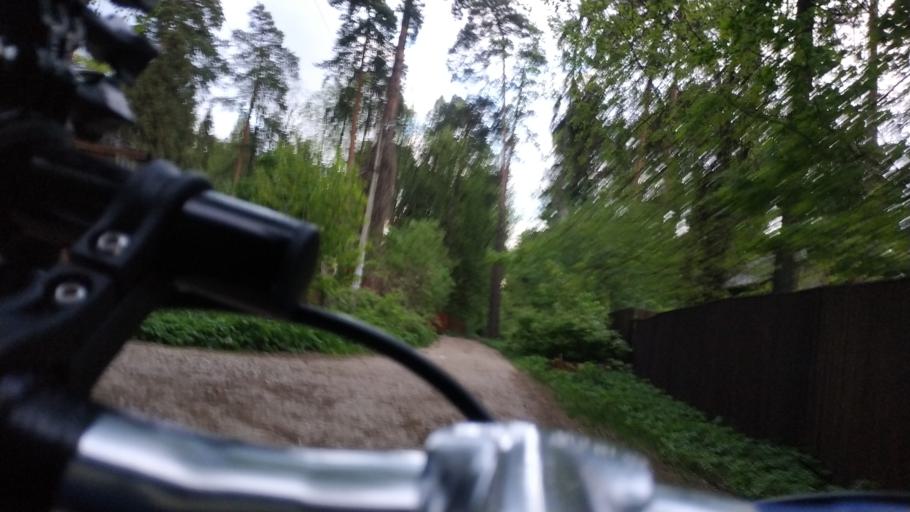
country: RU
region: Moskovskaya
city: Kratovo
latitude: 55.6099
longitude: 38.1612
